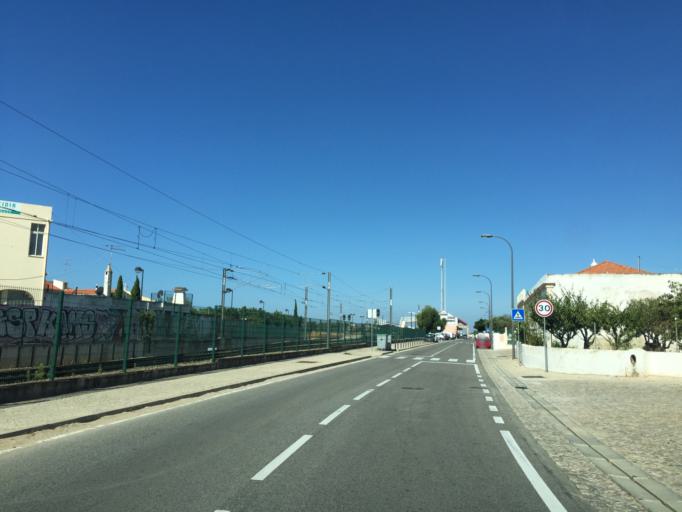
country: PT
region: Faro
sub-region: Loule
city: Almancil
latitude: 37.1039
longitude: -8.0554
